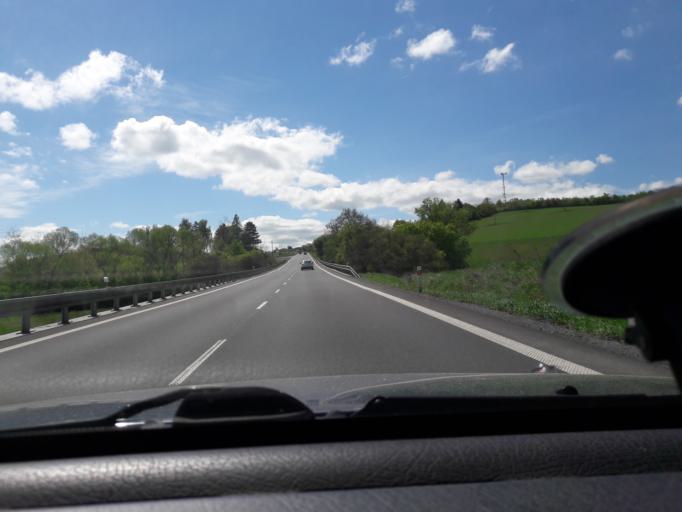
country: SK
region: Banskobystricky
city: Krupina
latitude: 48.4572
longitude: 19.0966
